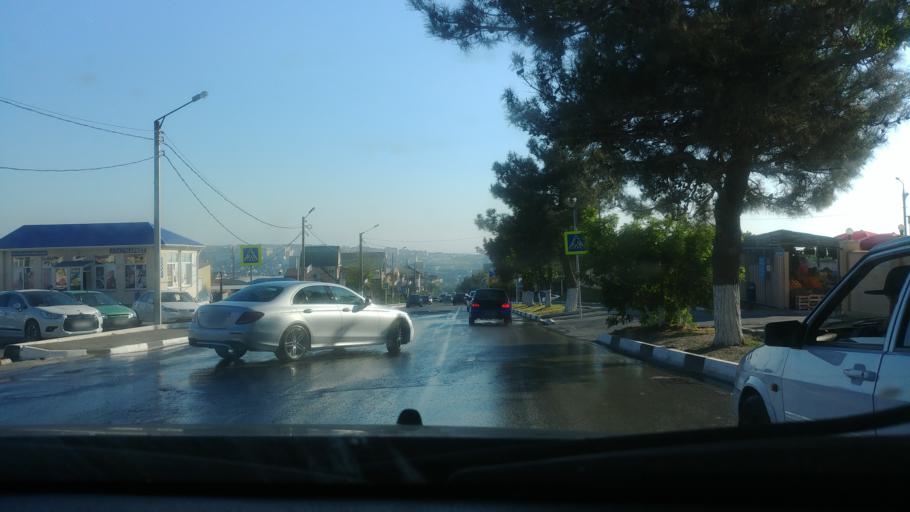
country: RU
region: Krasnodarskiy
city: Gelendzhik
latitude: 44.5707
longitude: 38.0922
